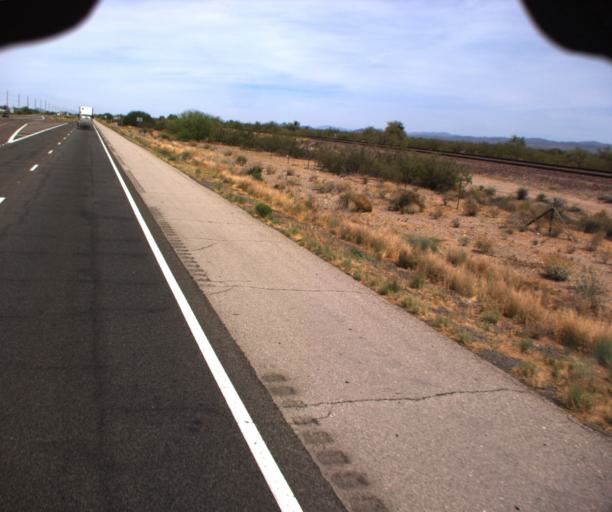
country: US
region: Arizona
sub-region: Maricopa County
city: Sun City West
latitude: 33.7833
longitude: -112.5354
